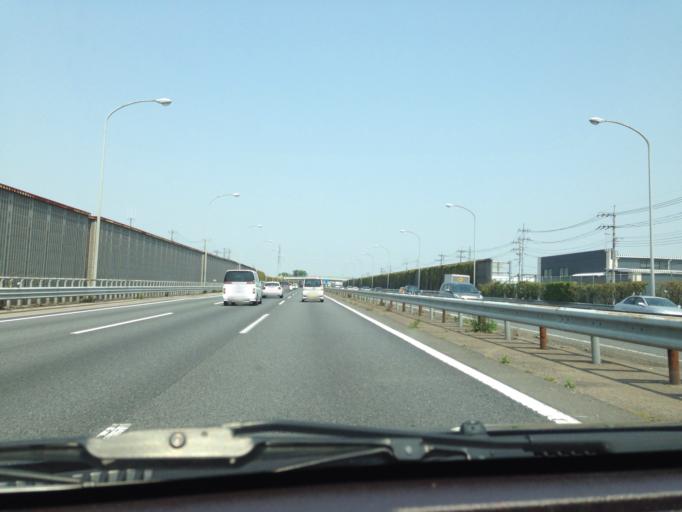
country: JP
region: Saitama
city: Iwatsuki
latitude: 35.9069
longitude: 139.7106
